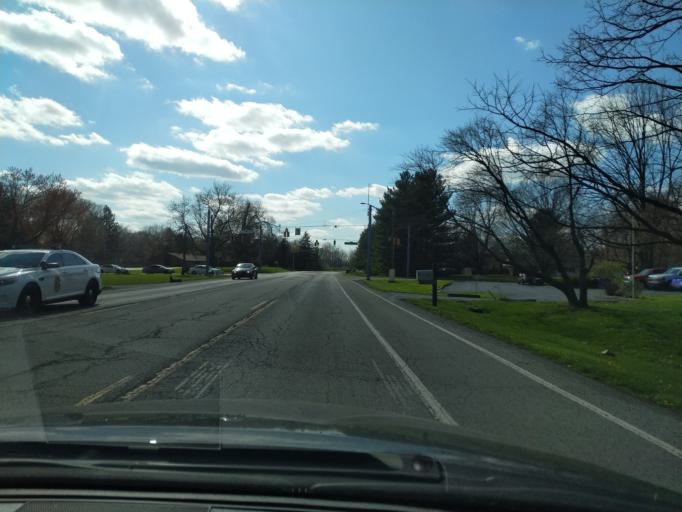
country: US
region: Indiana
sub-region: Marion County
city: Meridian Hills
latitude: 39.8854
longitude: -86.1877
